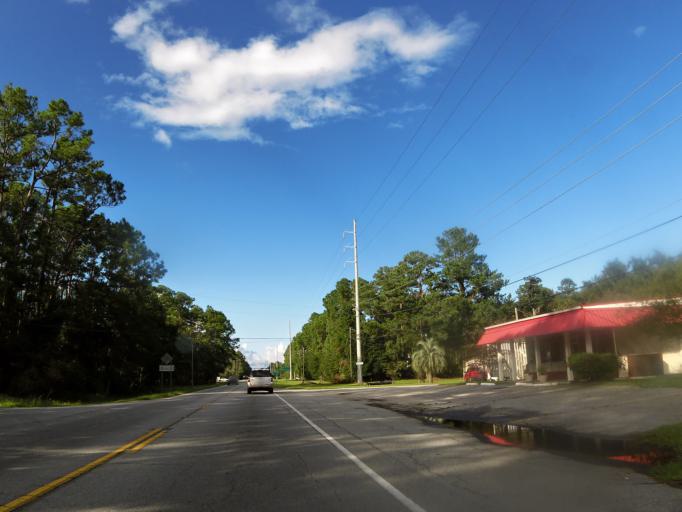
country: US
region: Georgia
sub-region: Glynn County
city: Country Club Estates
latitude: 31.2528
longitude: -81.4439
